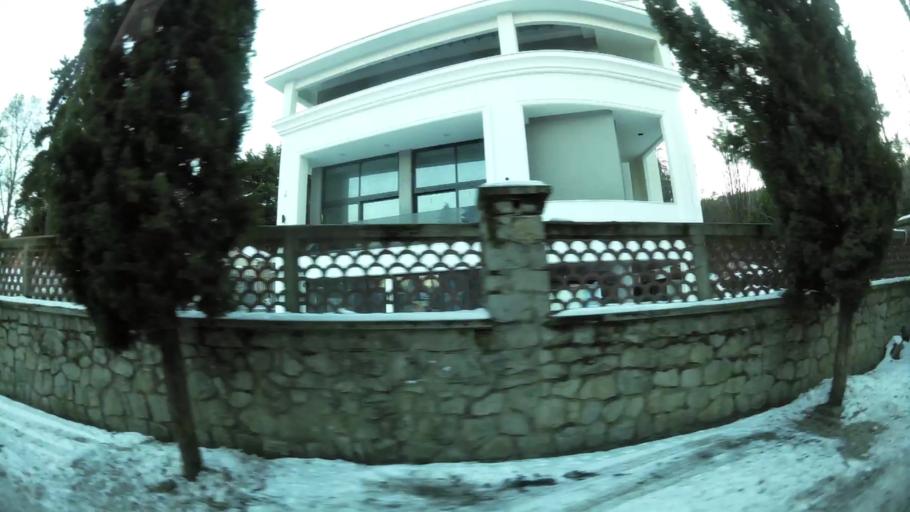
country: MK
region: Karpos
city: Skopje
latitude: 41.9886
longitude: 21.4134
